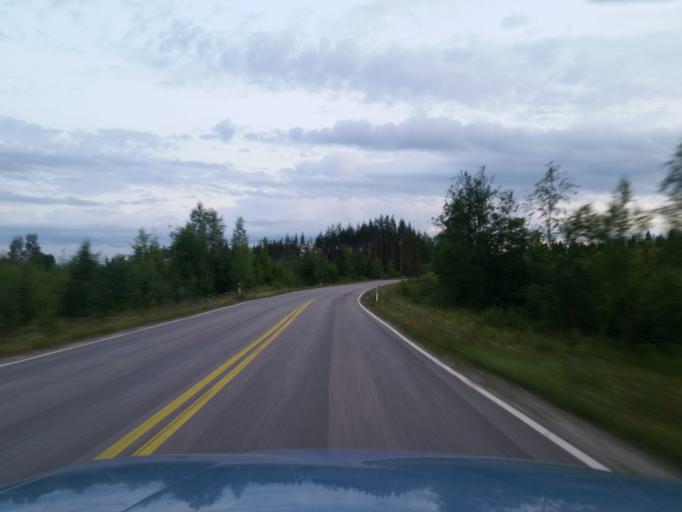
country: FI
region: Southern Savonia
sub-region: Savonlinna
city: Sulkava
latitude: 61.8116
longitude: 28.4293
